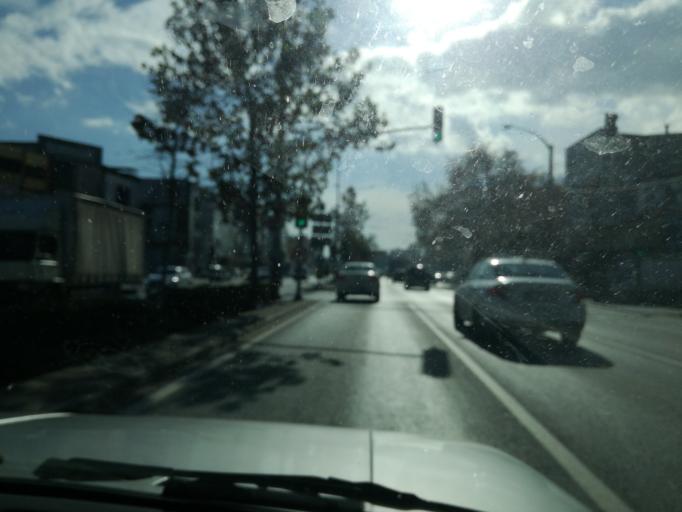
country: TR
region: Izmir
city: Karabaglar
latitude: 38.3769
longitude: 27.1349
